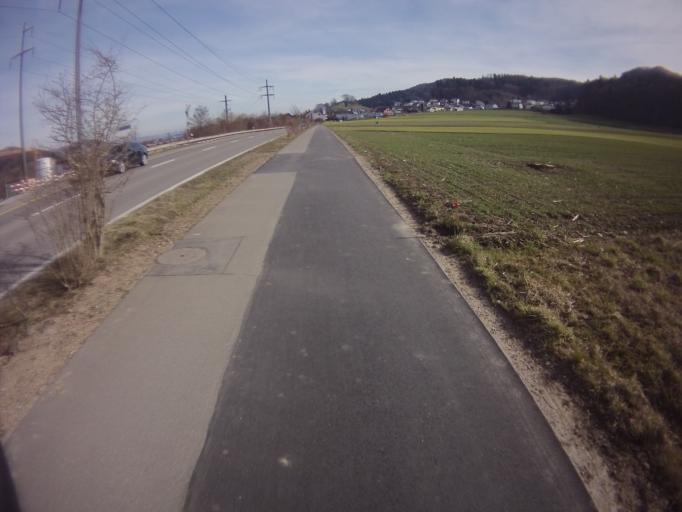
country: CH
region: Aargau
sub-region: Bezirk Baden
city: Killwangen
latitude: 47.4380
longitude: 8.3417
